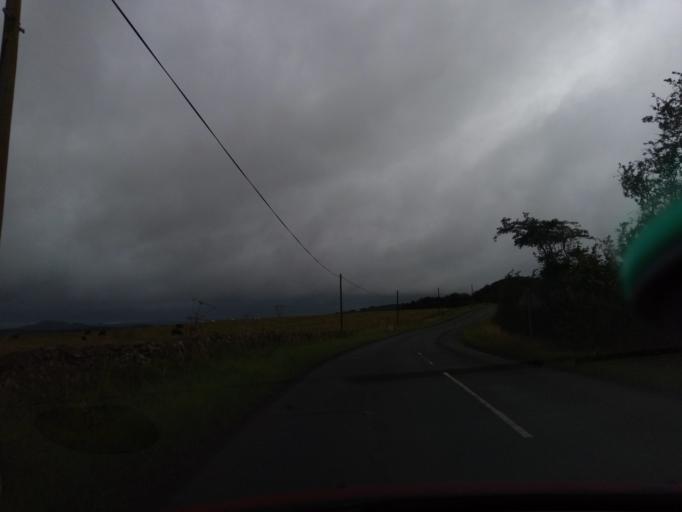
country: GB
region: Scotland
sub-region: The Scottish Borders
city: Kelso
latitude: 55.6377
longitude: -2.5298
